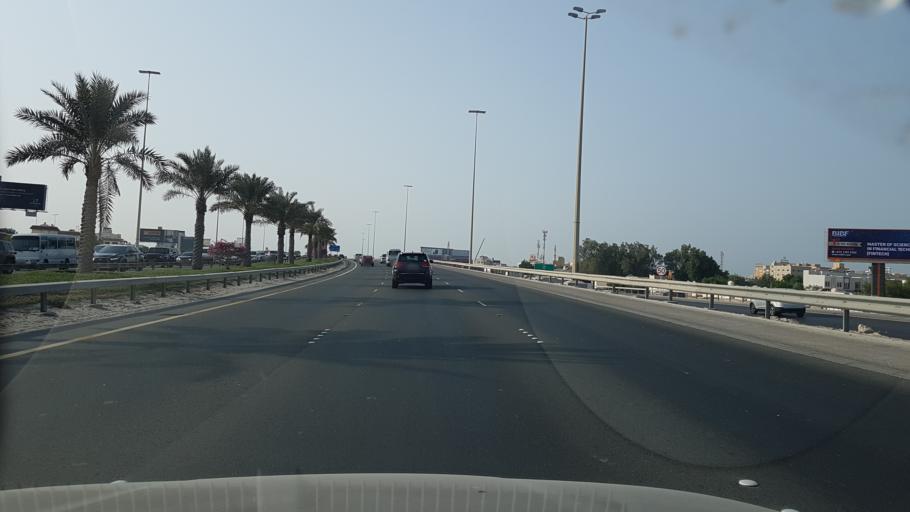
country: BH
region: Manama
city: Jidd Hafs
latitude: 26.2218
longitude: 50.5222
